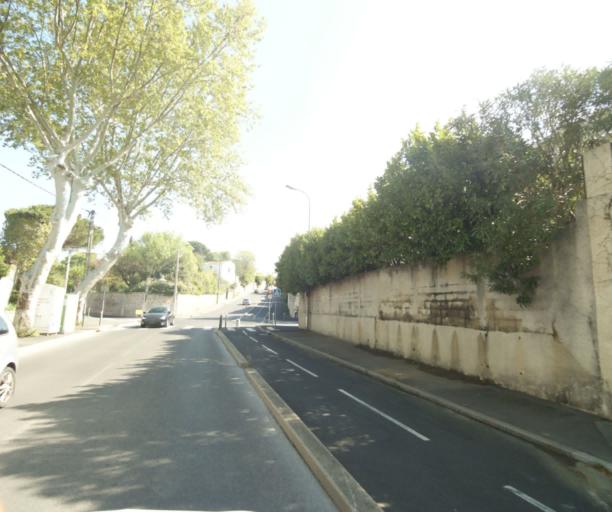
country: FR
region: Languedoc-Roussillon
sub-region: Departement de l'Herault
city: Castelnau-le-Lez
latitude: 43.6111
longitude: 3.9005
